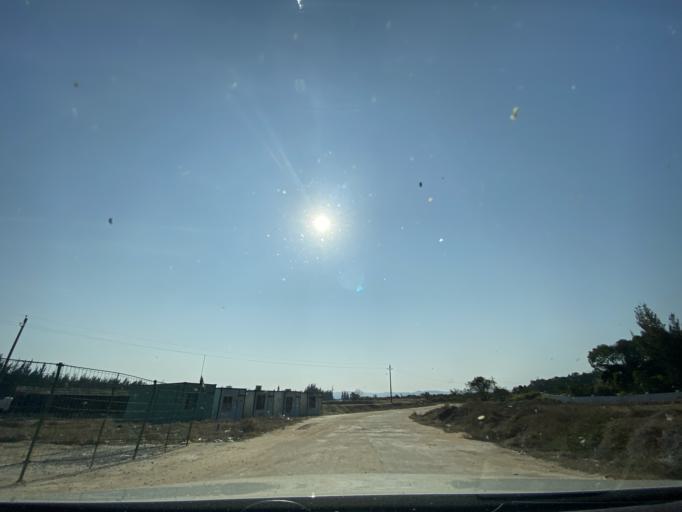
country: CN
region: Hainan
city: Haitangwan
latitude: 18.3970
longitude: 109.7707
